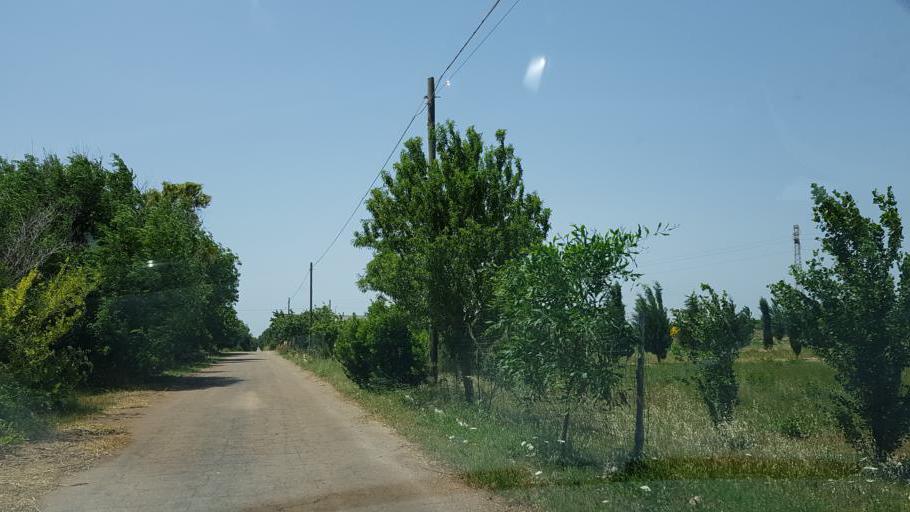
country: IT
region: Apulia
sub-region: Provincia di Lecce
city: Porto Cesareo
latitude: 40.3254
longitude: 17.8661
